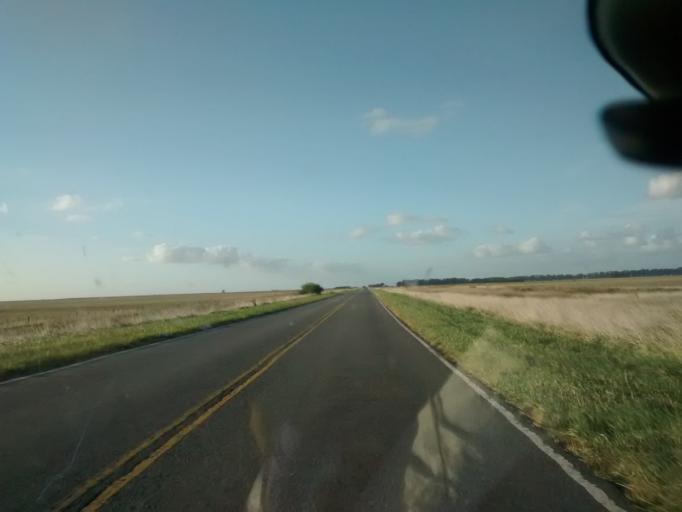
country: AR
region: Buenos Aires
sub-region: Partido de General Belgrano
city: General Belgrano
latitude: -36.0665
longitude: -58.6257
